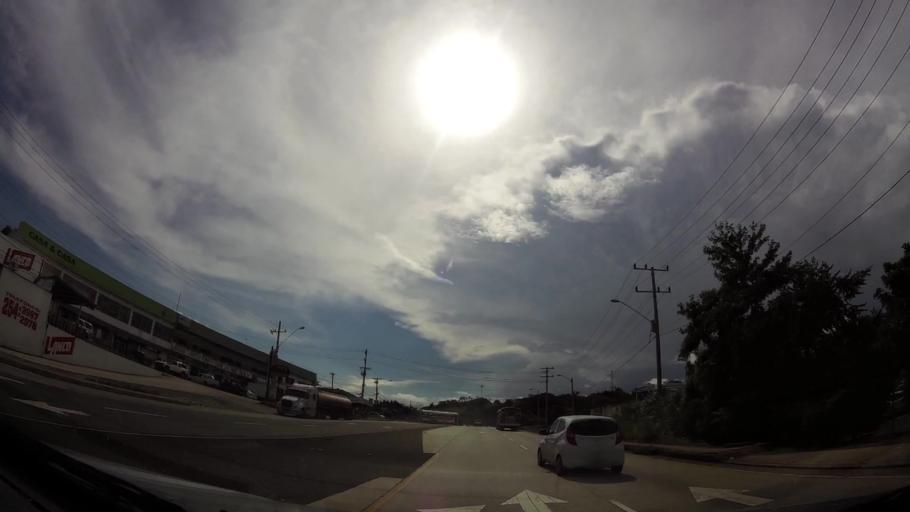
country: PA
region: Panama
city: La Chorrera
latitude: 8.8948
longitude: -79.7605
